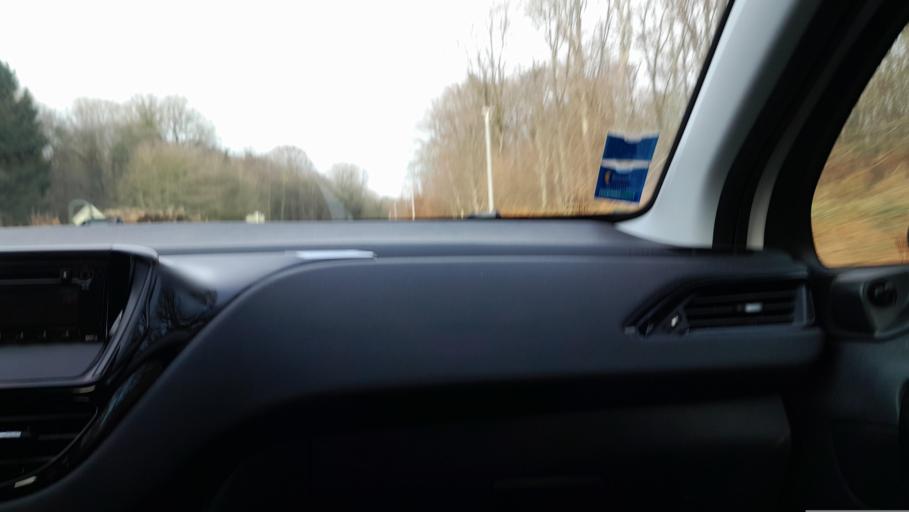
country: FR
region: Brittany
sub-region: Departement d'Ille-et-Vilaine
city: La Guerche-de-Bretagne
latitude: 47.9050
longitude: -1.1870
